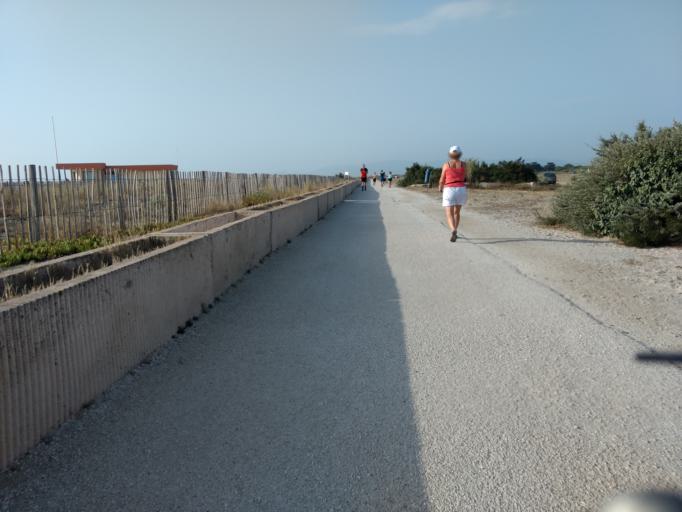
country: FR
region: Languedoc-Roussillon
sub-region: Departement des Pyrenees-Orientales
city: Le Barcares
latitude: 42.7829
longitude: 3.0381
